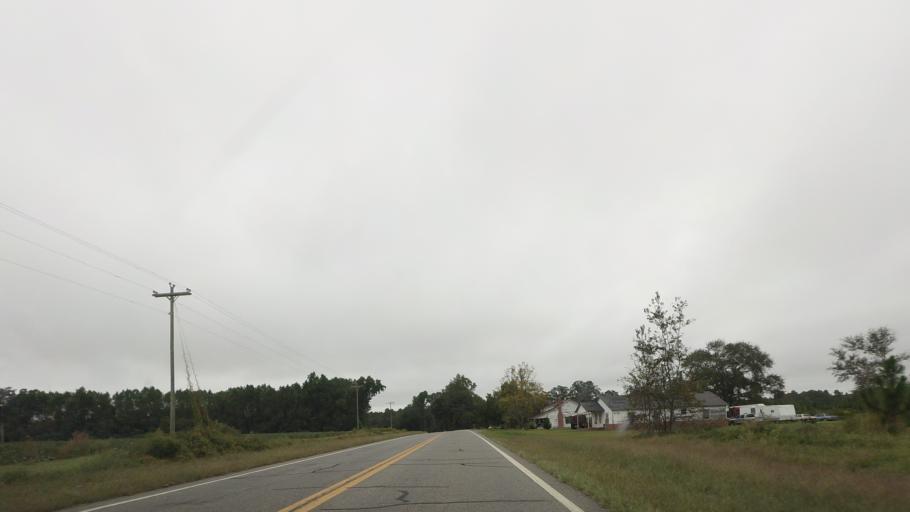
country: US
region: Georgia
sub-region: Irwin County
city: Ocilla
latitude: 31.5097
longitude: -83.2390
